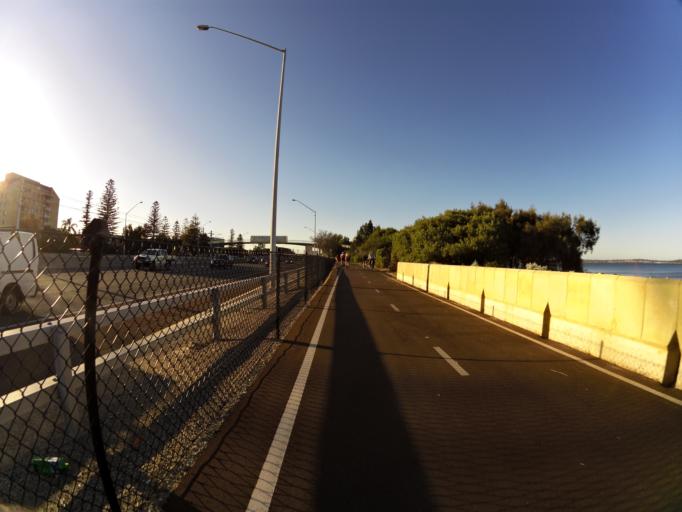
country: AU
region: Western Australia
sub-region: South Perth
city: South Perth
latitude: -31.9752
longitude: 115.8478
